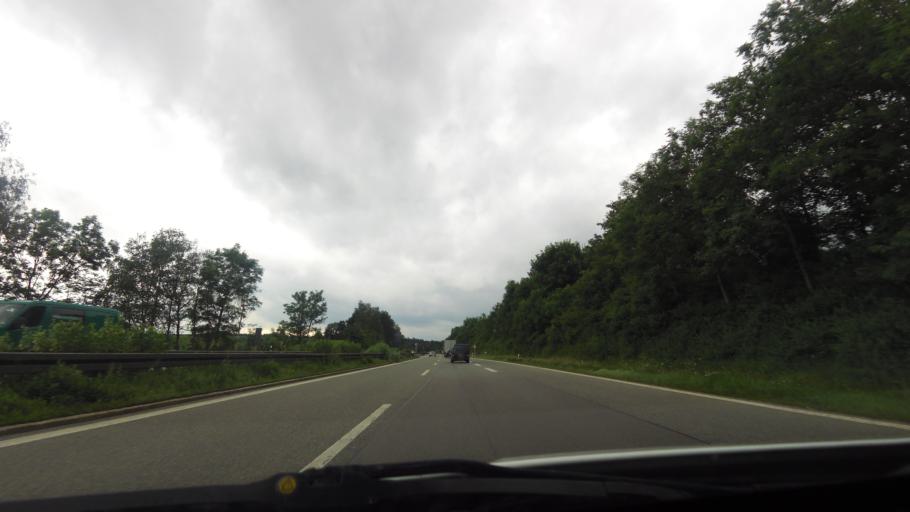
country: DE
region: Bavaria
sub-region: Swabia
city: Buxheim
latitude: 47.9928
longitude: 10.1419
